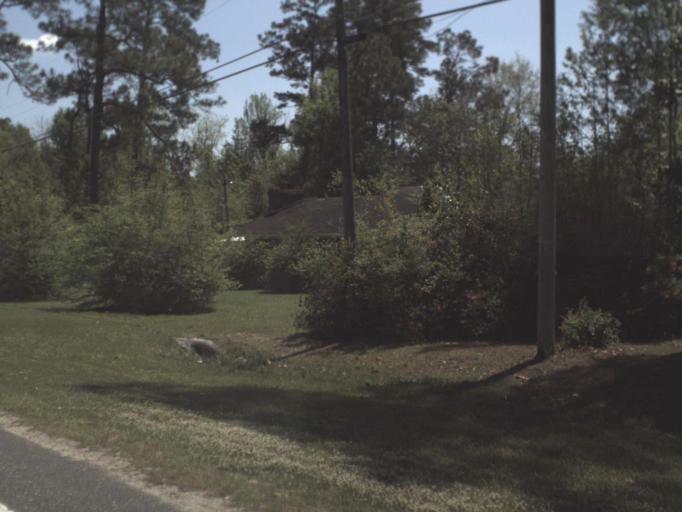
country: US
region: Florida
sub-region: Escambia County
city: Century
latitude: 30.9789
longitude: -87.2523
